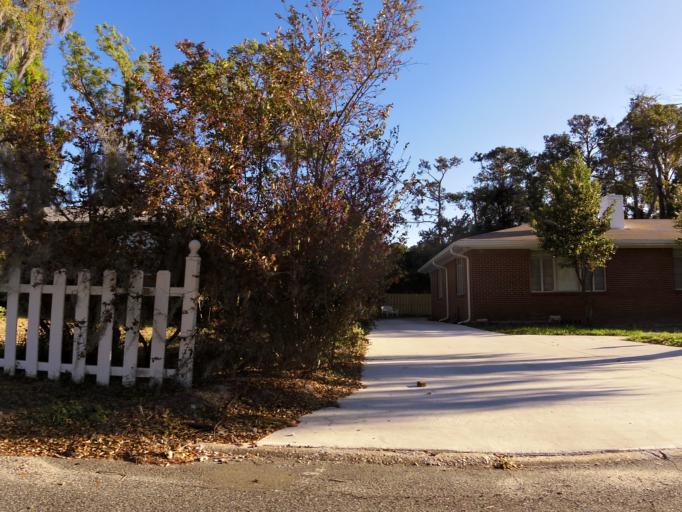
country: US
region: Florida
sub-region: Duval County
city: Jacksonville
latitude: 30.2598
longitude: -81.6458
